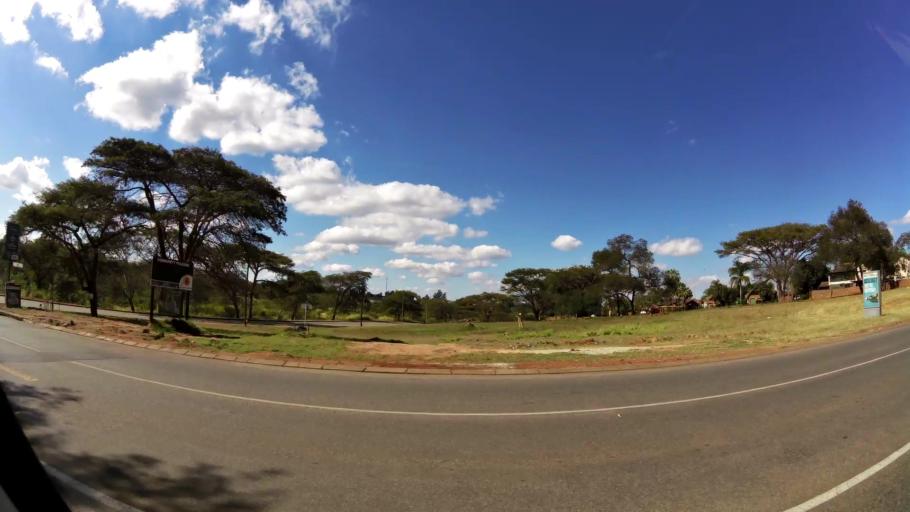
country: ZA
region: Limpopo
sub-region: Mopani District Municipality
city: Tzaneen
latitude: -23.8173
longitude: 30.1585
